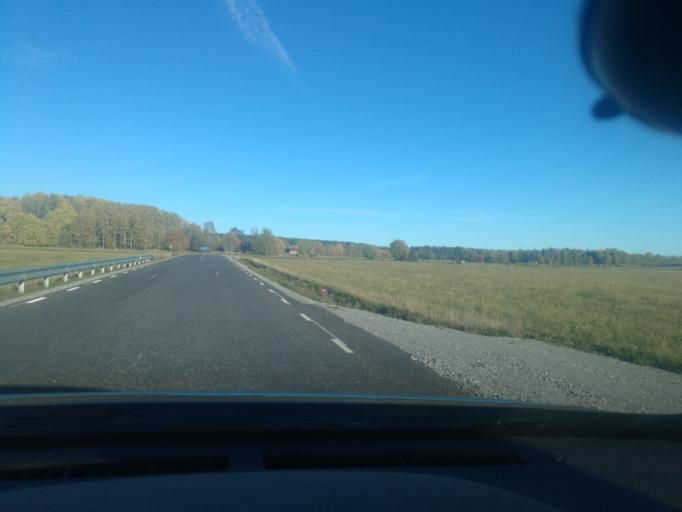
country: SE
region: Vaestmanland
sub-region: Kopings Kommun
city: Koping
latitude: 59.5726
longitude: 16.0822
